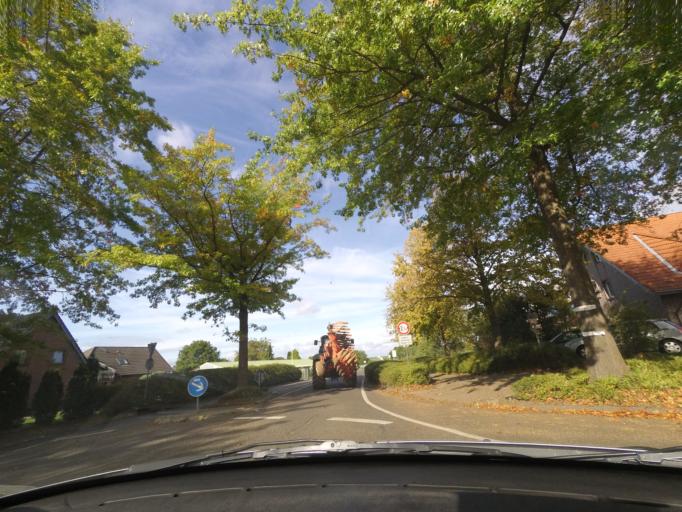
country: DE
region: North Rhine-Westphalia
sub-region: Regierungsbezirk Dusseldorf
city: Korschenbroich
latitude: 51.1482
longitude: 6.5483
